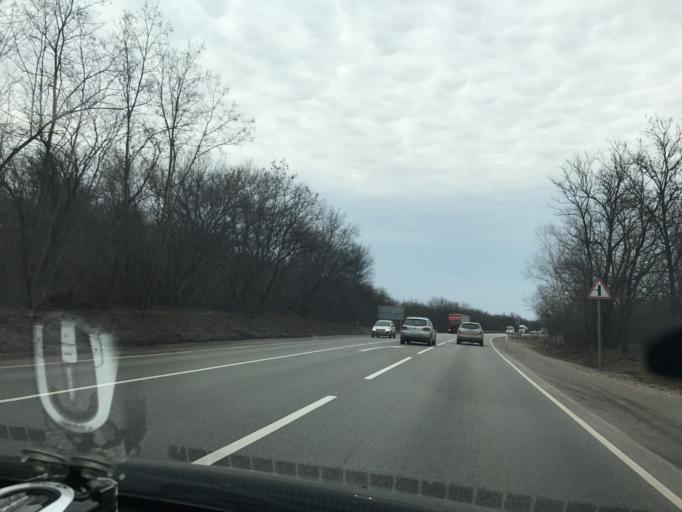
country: RU
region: Krasnodarskiy
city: Novoukrainskoye
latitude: 45.4034
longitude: 40.5467
